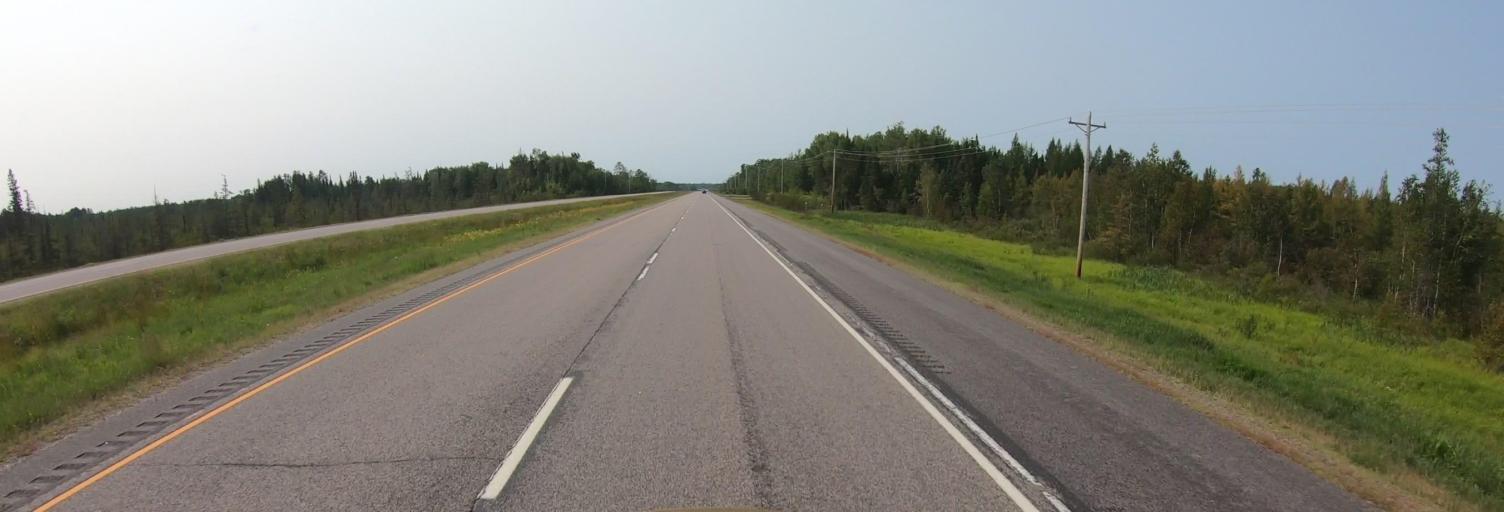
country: US
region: Minnesota
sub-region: Saint Louis County
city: Parkville
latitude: 47.6217
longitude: -92.5539
